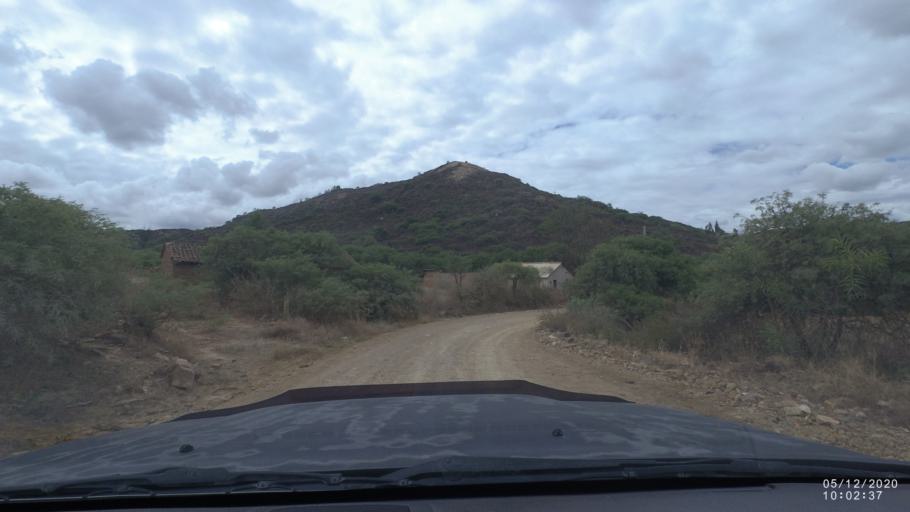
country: BO
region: Cochabamba
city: Sipe Sipe
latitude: -17.4516
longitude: -66.2848
